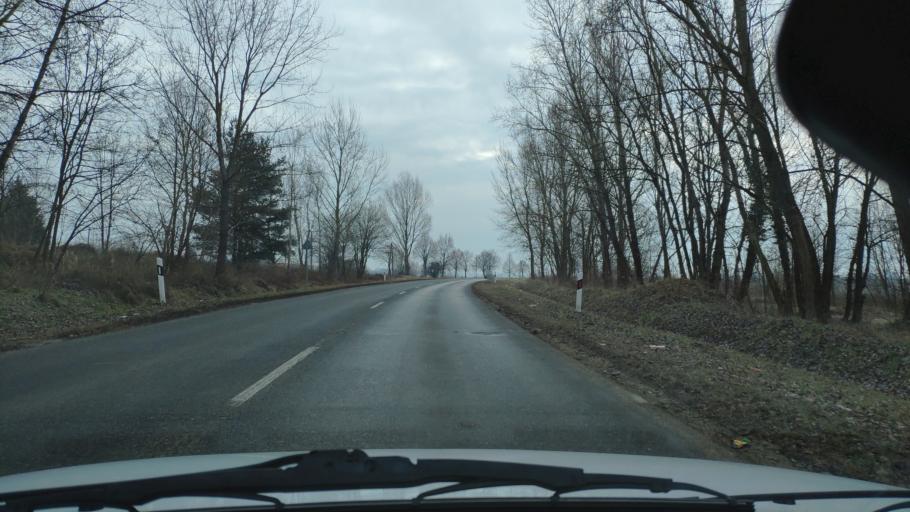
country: HU
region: Zala
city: Nagykanizsa
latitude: 46.5129
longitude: 16.9824
